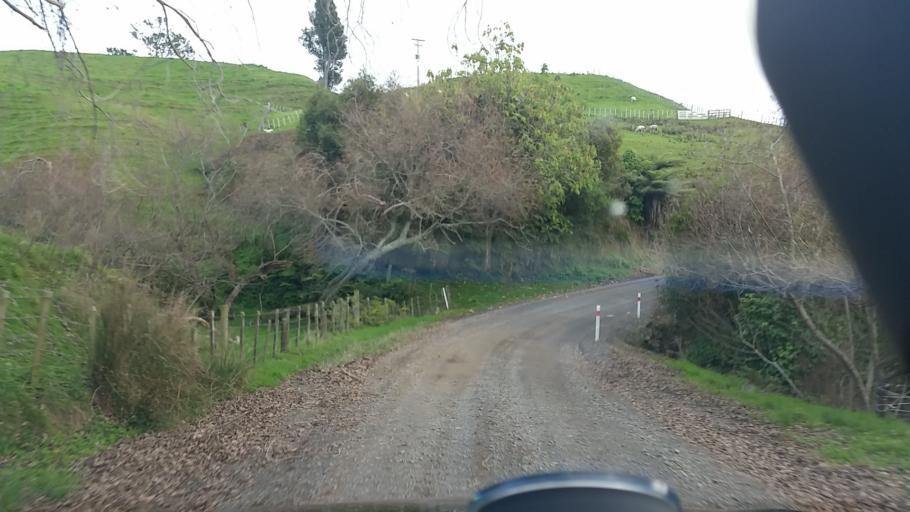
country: NZ
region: Waikato
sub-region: Matamata-Piako District
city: Matamata
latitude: -37.8248
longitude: 175.6764
